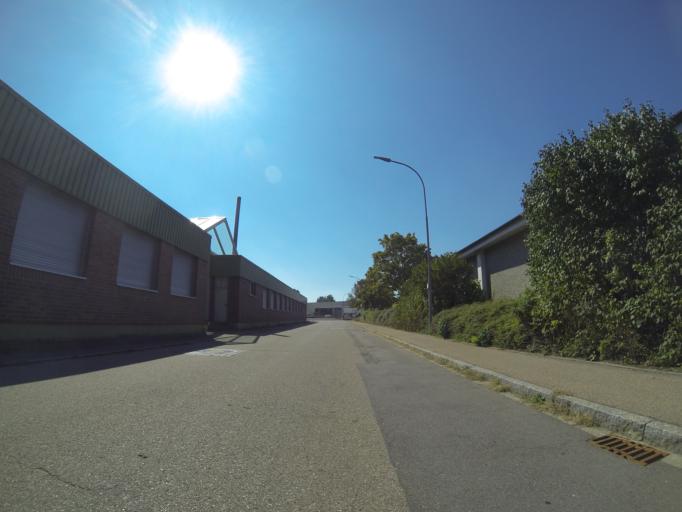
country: DE
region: Baden-Wuerttemberg
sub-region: Tuebingen Region
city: Erbach
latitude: 48.3287
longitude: 9.9025
